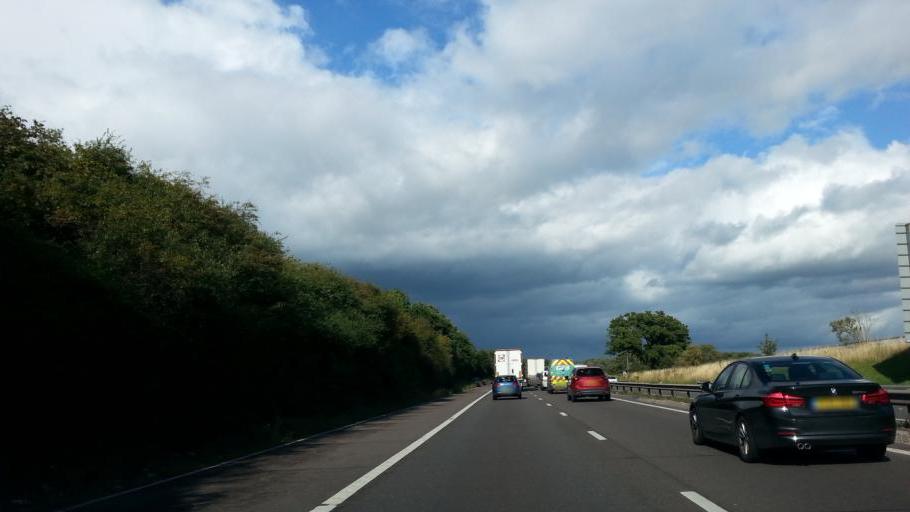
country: GB
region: England
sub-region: Warwickshire
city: Kingsbury
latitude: 52.5571
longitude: -1.7087
